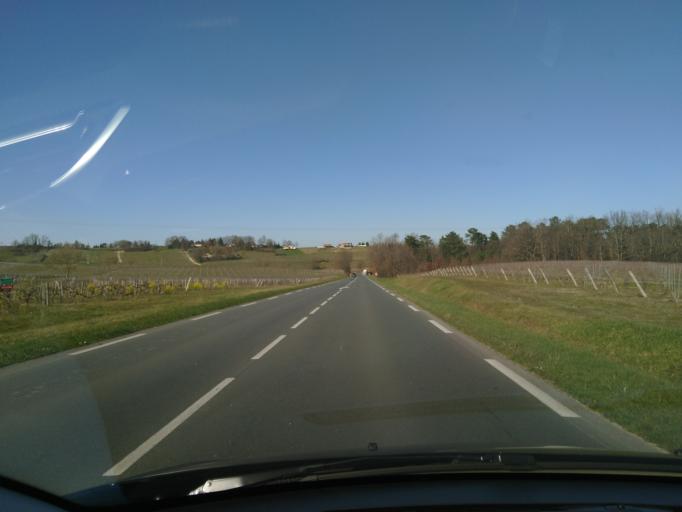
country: FR
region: Aquitaine
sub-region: Departement de la Dordogne
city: Monbazillac
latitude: 44.7829
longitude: 0.5260
